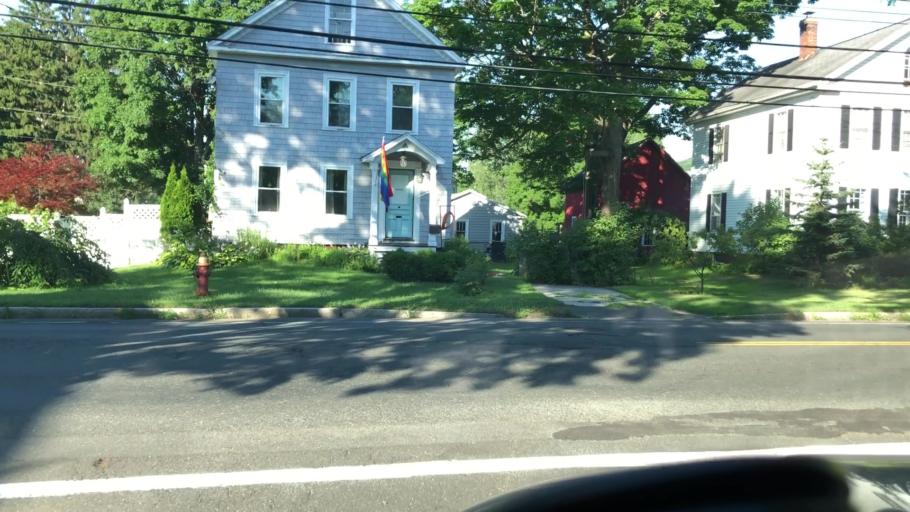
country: US
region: Massachusetts
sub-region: Hampshire County
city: Easthampton
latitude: 42.2625
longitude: -72.6627
